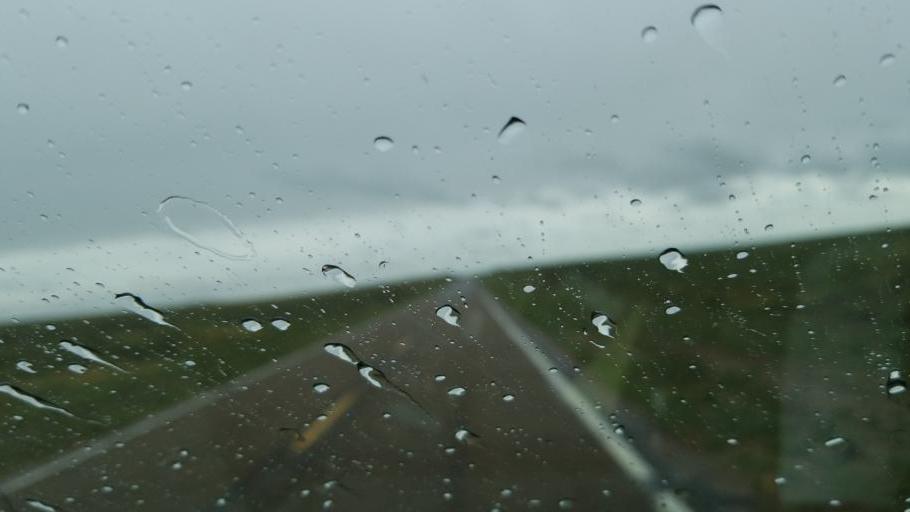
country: US
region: Colorado
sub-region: Lincoln County
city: Hugo
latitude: 38.8494
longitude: -103.2627
